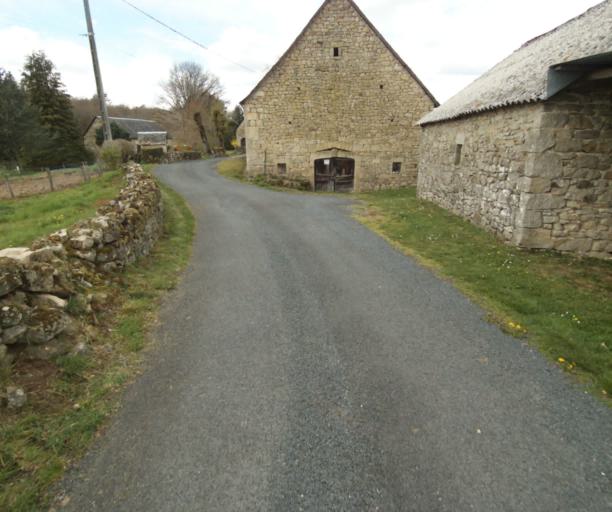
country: FR
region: Limousin
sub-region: Departement de la Correze
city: Argentat
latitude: 45.2126
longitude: 1.9188
